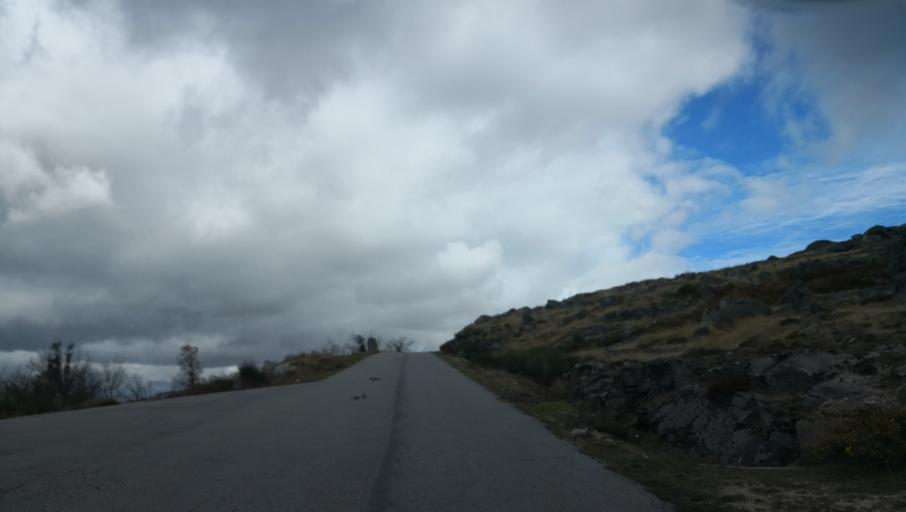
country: PT
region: Vila Real
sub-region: Vila Real
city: Vila Real
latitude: 41.3744
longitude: -7.8299
